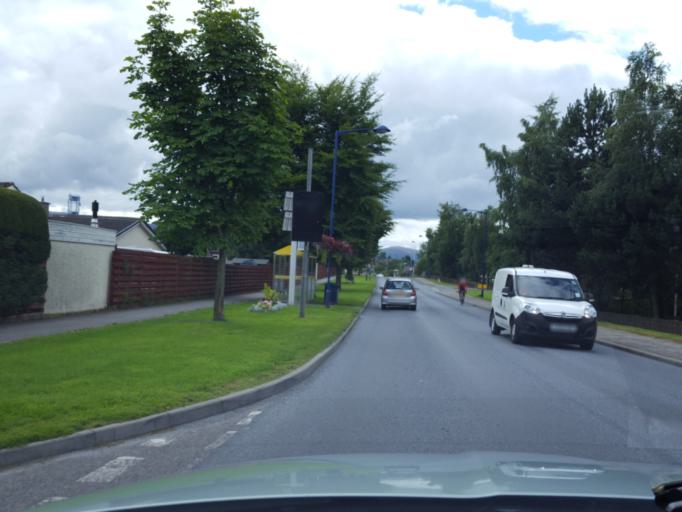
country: GB
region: Scotland
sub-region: Highland
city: Aviemore
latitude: 57.1999
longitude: -3.8284
